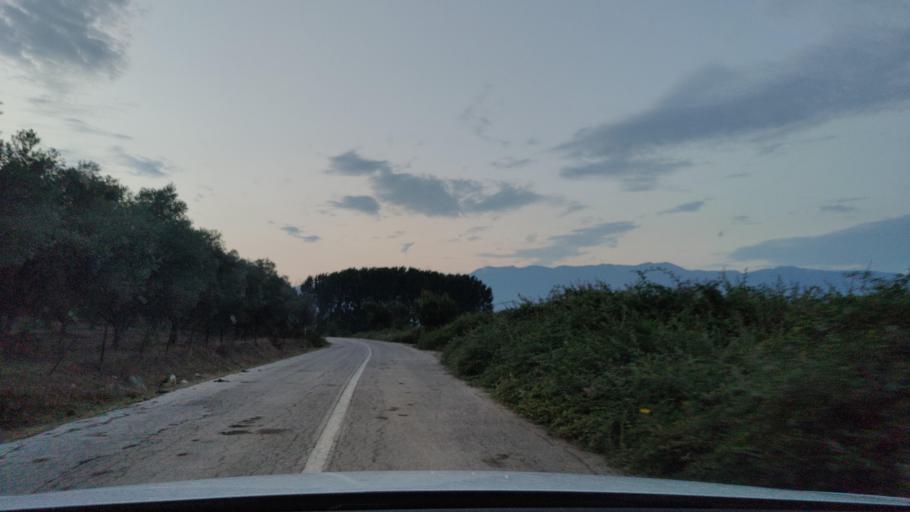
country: GR
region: Central Macedonia
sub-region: Nomos Serron
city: Chrysochorafa
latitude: 41.1597
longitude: 23.1900
